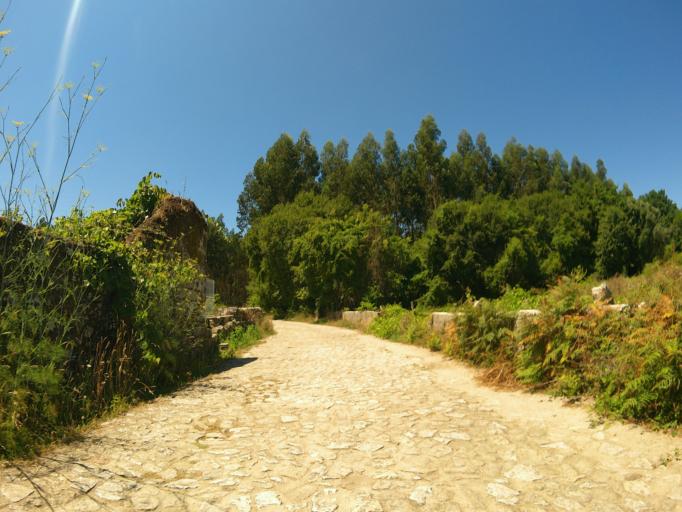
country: PT
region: Viana do Castelo
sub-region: Viana do Castelo
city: Darque
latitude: 41.7018
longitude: -8.7583
